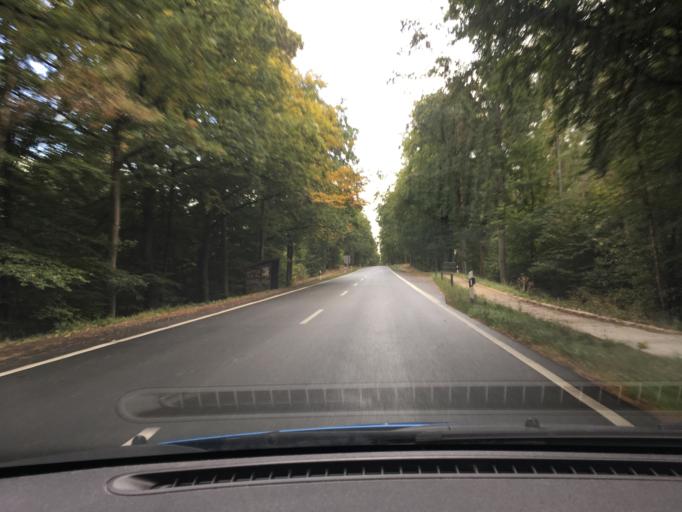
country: DE
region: Lower Saxony
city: Schnega
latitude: 52.9236
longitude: 10.8572
